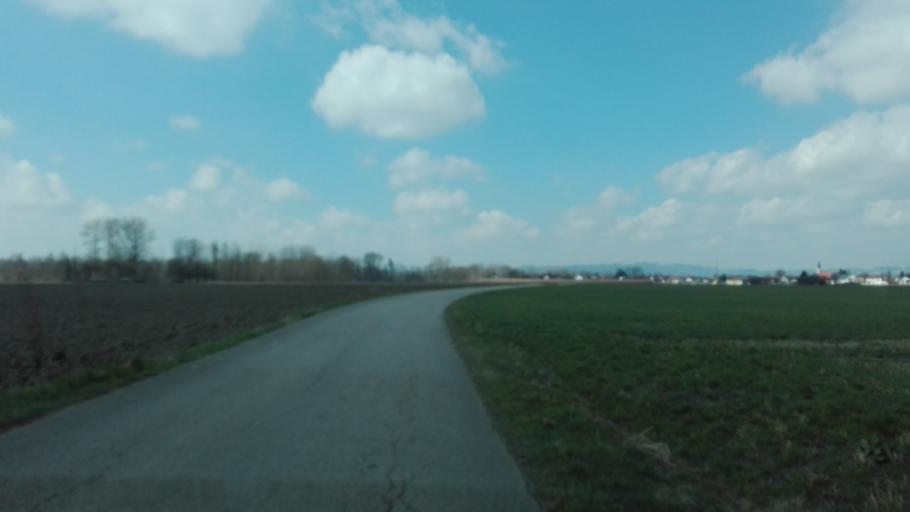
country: AT
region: Upper Austria
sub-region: Politischer Bezirk Urfahr-Umgebung
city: Goldworth
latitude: 48.3210
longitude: 14.1137
